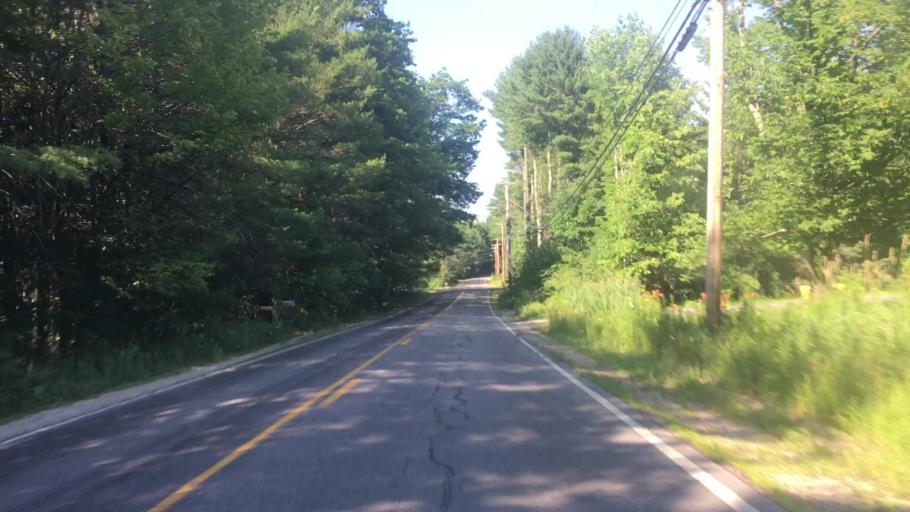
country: US
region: Maine
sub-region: York County
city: Hollis Center
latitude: 43.6718
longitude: -70.5976
